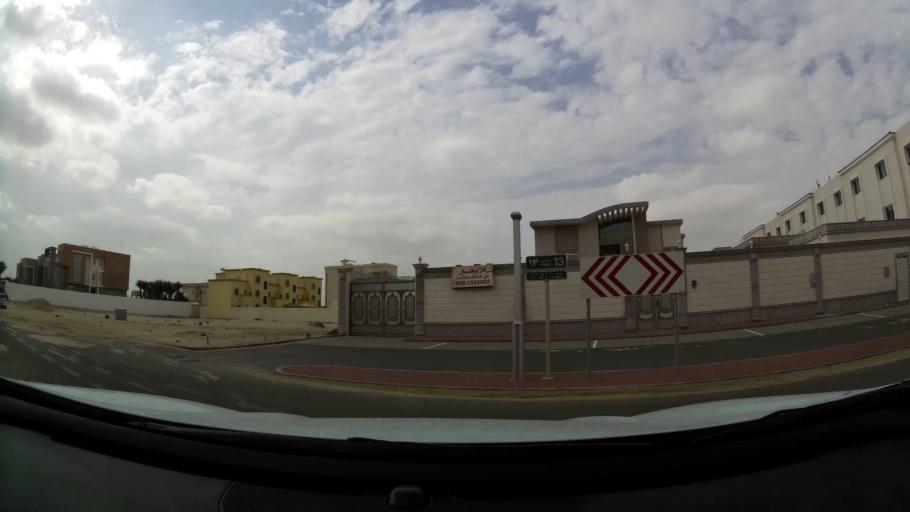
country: AE
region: Abu Dhabi
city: Abu Dhabi
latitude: 24.3837
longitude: 54.6381
